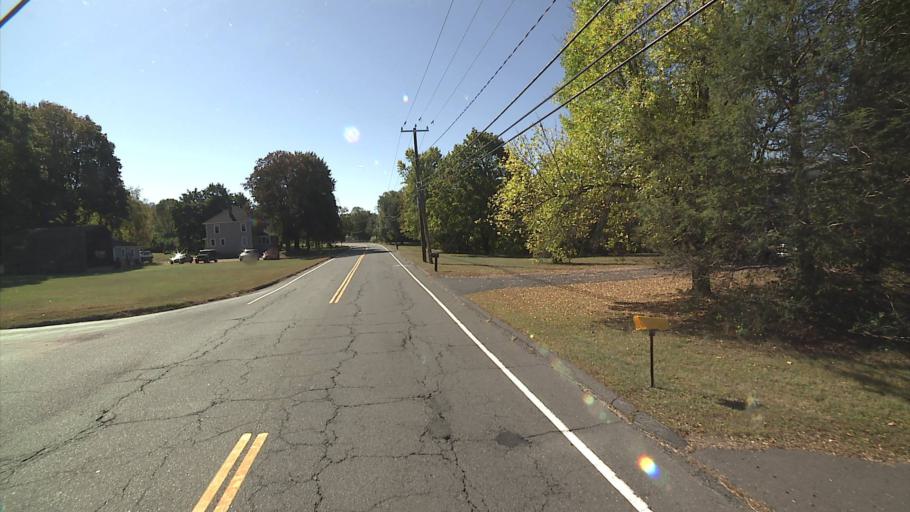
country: US
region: Connecticut
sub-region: Tolland County
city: Somers
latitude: 41.9728
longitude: -72.4437
